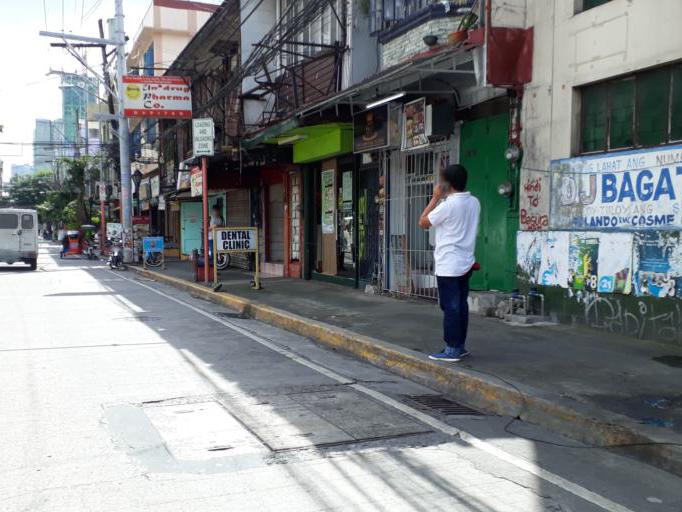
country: PH
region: Metro Manila
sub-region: City of Manila
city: Manila
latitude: 14.6161
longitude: 120.9931
